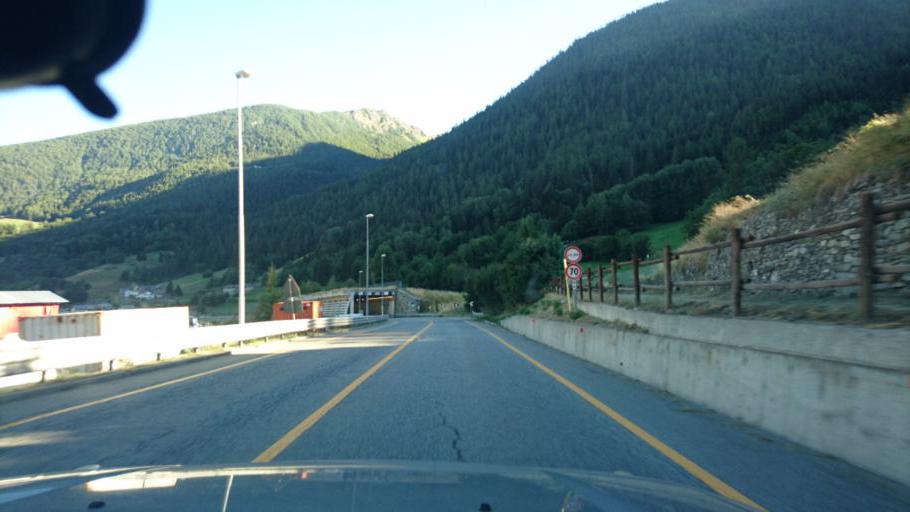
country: IT
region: Aosta Valley
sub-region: Valle d'Aosta
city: Etroubles
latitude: 45.8141
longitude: 7.2378
